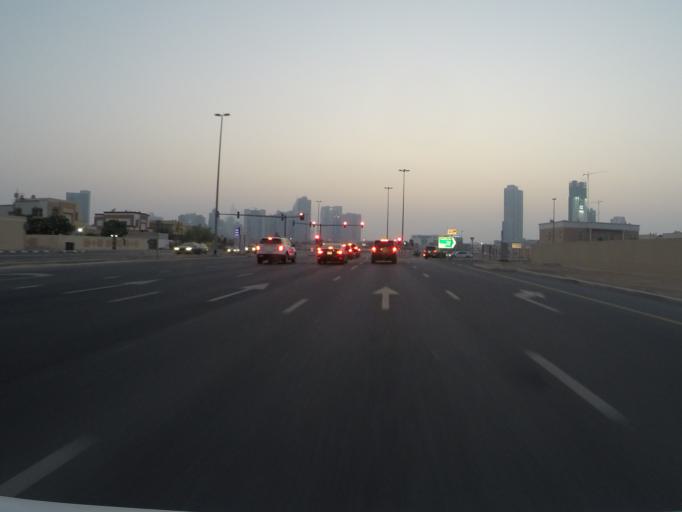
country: AE
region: Dubai
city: Dubai
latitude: 25.1055
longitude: 55.1915
